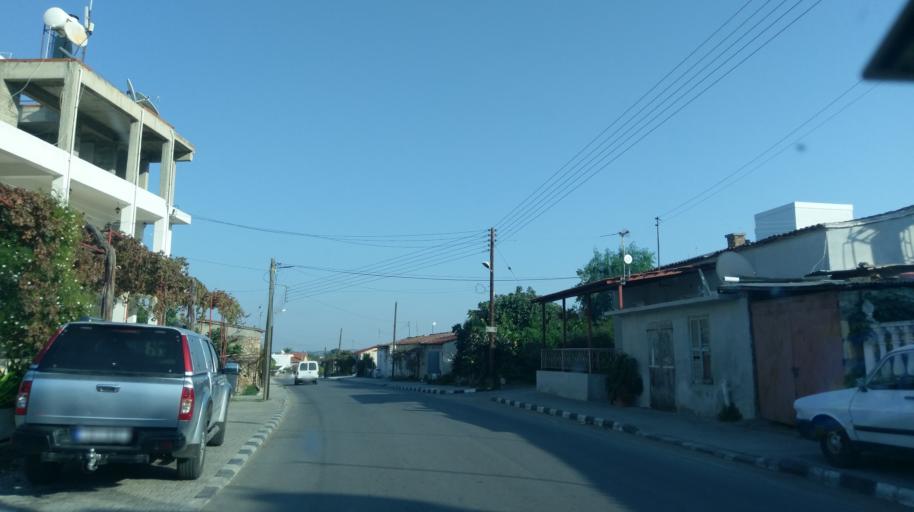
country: CY
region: Lefkosia
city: Lefka
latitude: 35.1429
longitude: 32.8091
